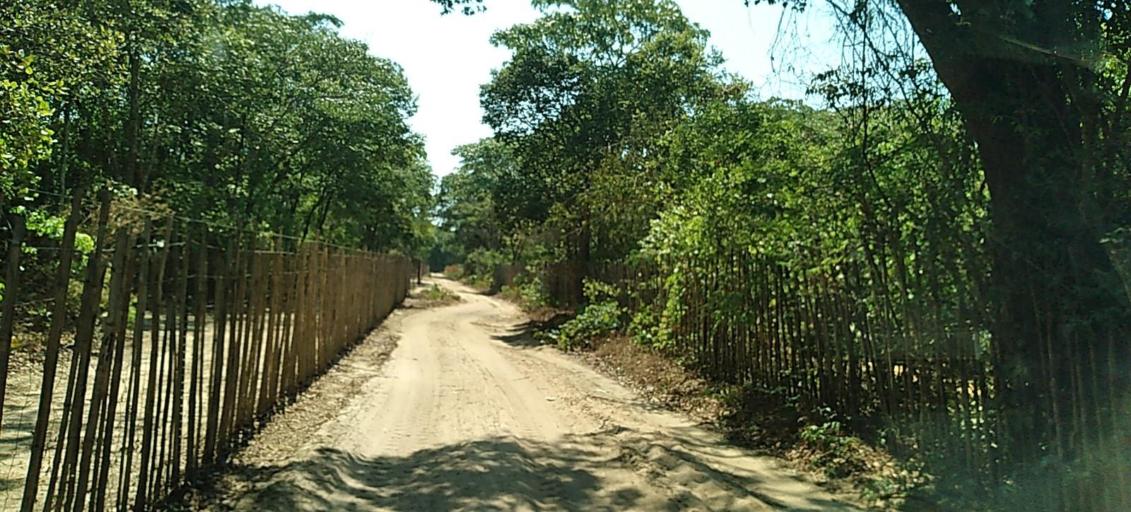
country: ZM
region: Copperbelt
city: Luanshya
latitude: -13.0095
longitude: 28.4640
